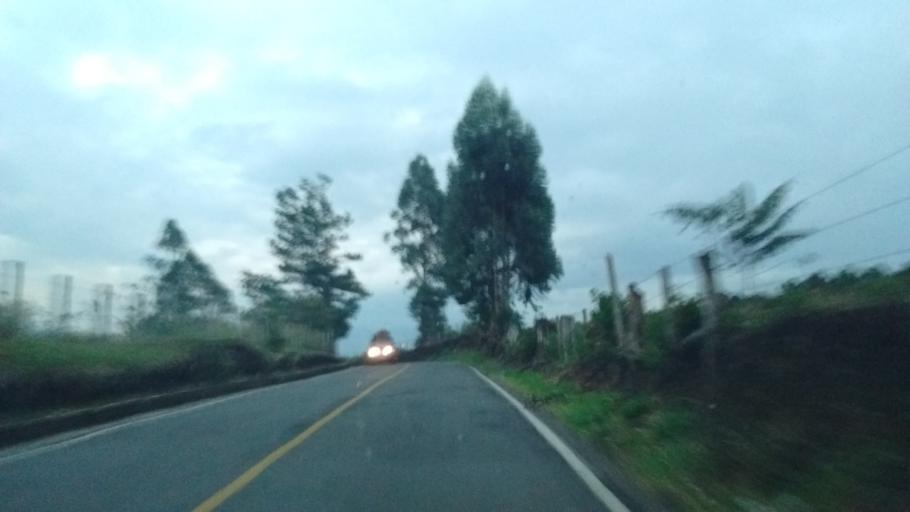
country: CO
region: Cauca
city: Popayan
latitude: 2.3687
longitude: -76.6935
